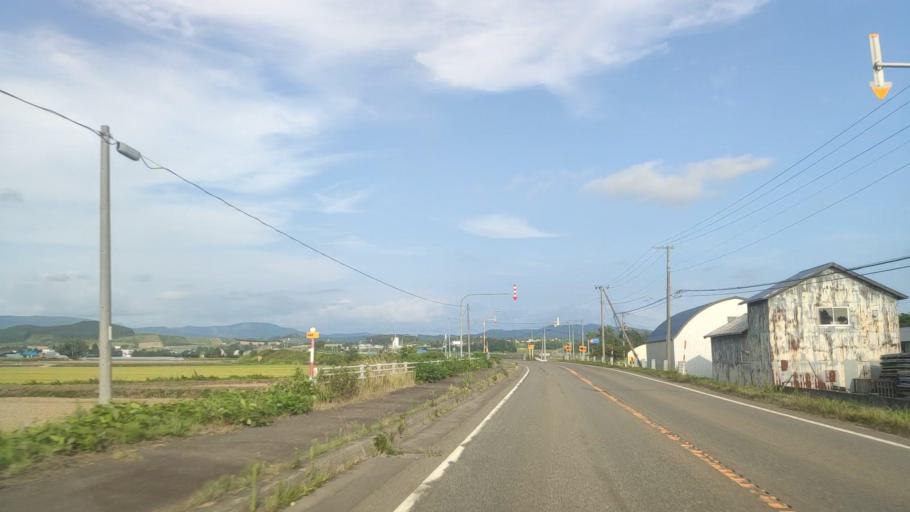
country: JP
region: Hokkaido
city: Iwamizawa
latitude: 43.0273
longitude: 141.8213
